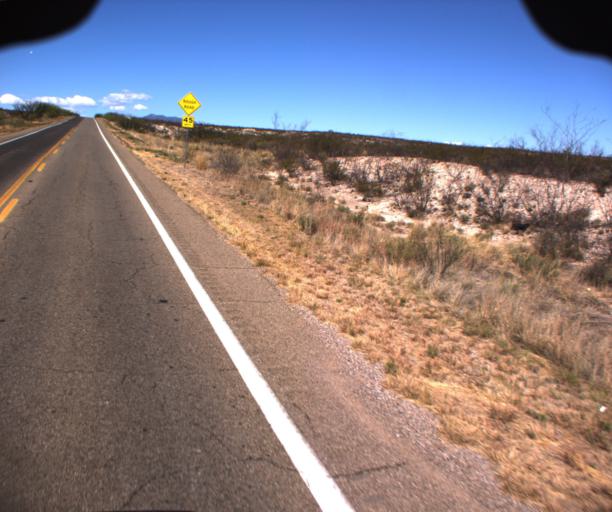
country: US
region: Arizona
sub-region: Cochise County
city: Sierra Vista Southeast
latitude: 31.5494
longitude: -110.1460
